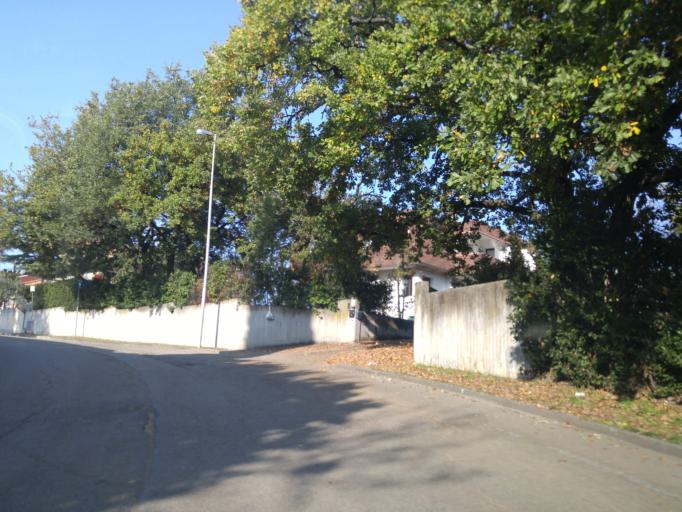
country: IT
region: The Marches
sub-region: Provincia di Pesaro e Urbino
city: Calcinelli
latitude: 43.7551
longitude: 12.9211
